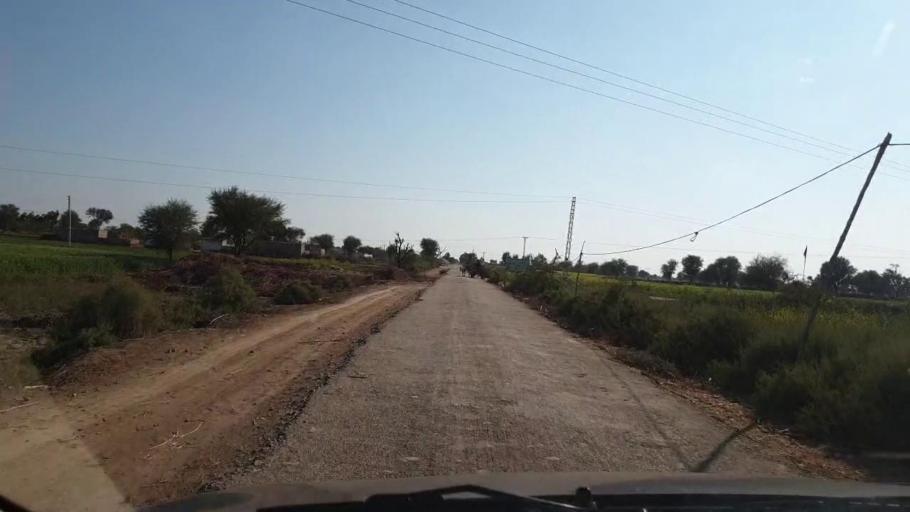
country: PK
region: Sindh
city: Sinjhoro
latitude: 25.9877
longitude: 68.8394
